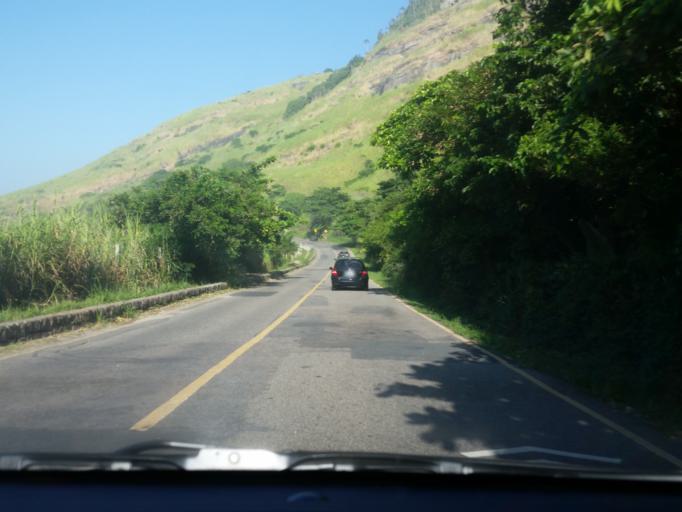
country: BR
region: Rio de Janeiro
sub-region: Nilopolis
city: Nilopolis
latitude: -23.0360
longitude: -43.4974
